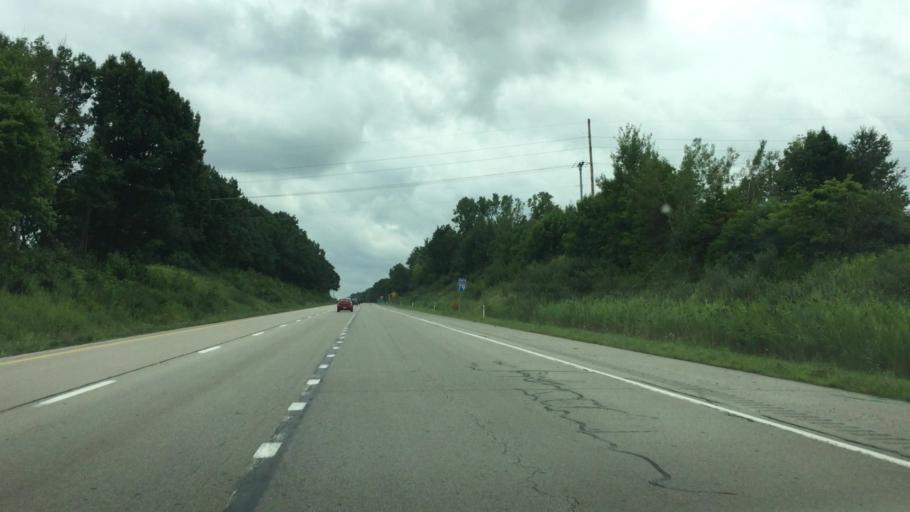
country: US
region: Pennsylvania
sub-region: Mercer County
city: Grove City
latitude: 41.1374
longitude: -80.1545
